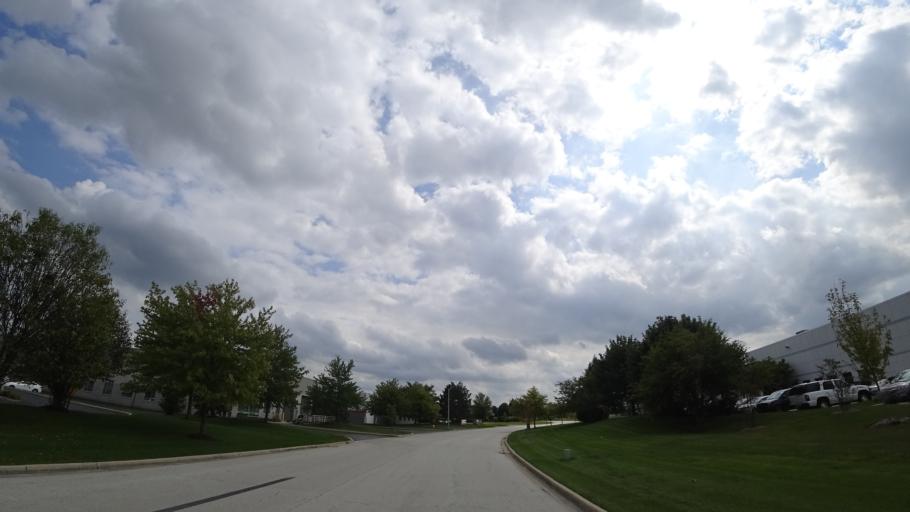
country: US
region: Illinois
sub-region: Cook County
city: Tinley Park
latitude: 41.5552
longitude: -87.8005
